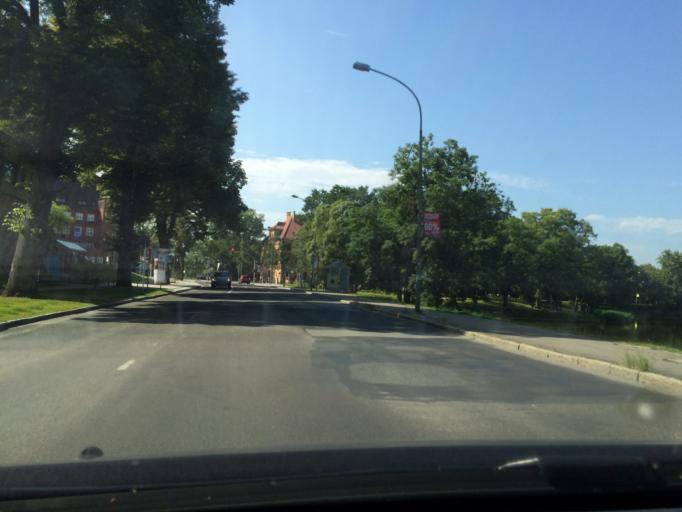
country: DE
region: Mecklenburg-Vorpommern
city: Stralsund
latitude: 54.3107
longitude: 13.0844
